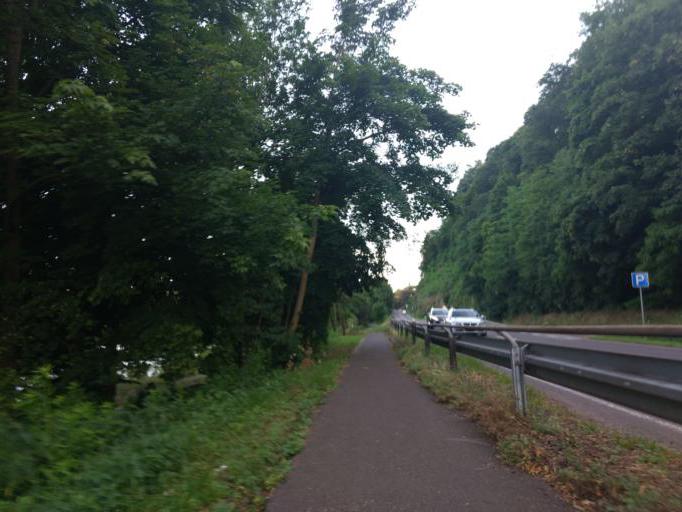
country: DE
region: Saarland
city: Wallerfangen
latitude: 49.3358
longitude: 6.7170
